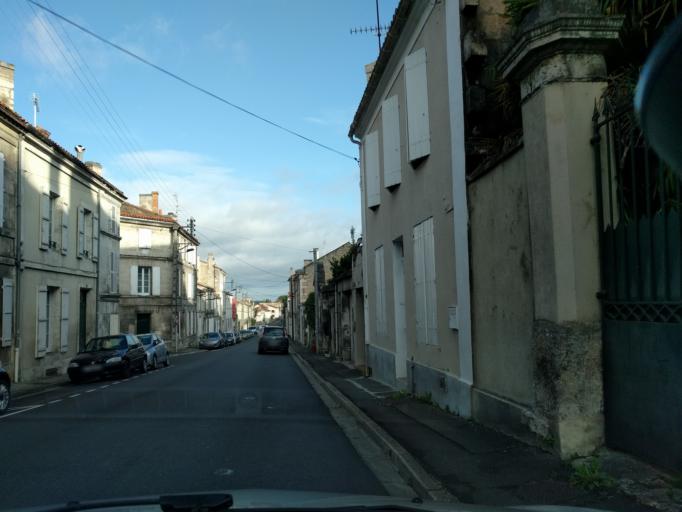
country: FR
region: Poitou-Charentes
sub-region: Departement de la Charente
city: Angouleme
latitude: 45.6449
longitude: 0.1547
